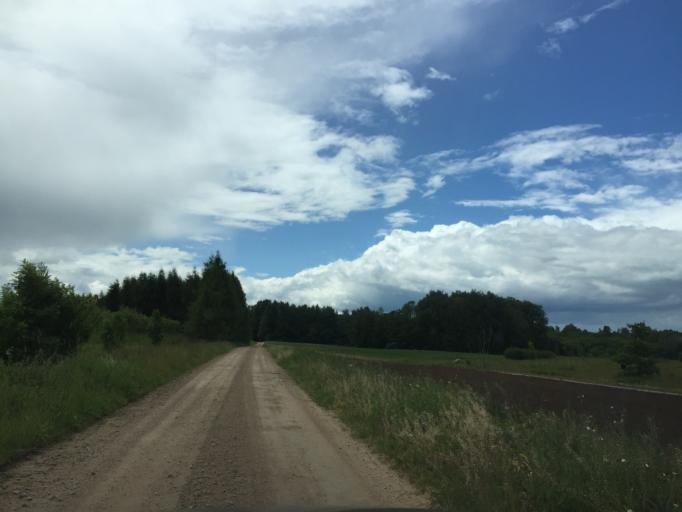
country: LV
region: Lecava
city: Iecava
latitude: 56.5573
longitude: 24.1598
